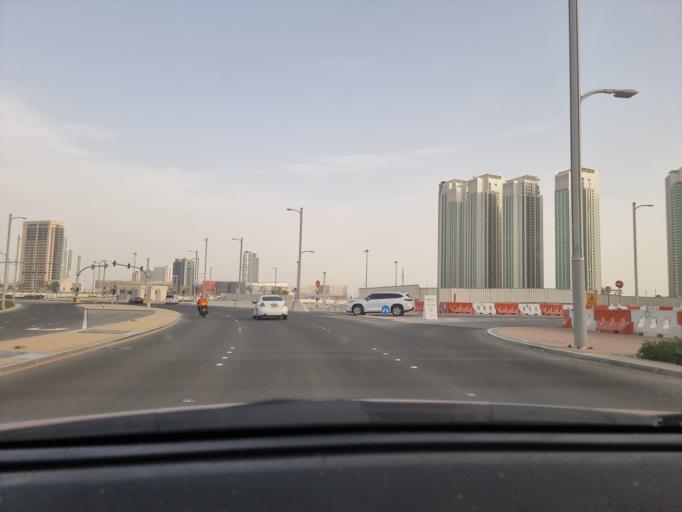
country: AE
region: Abu Dhabi
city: Abu Dhabi
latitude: 24.4976
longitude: 54.3955
